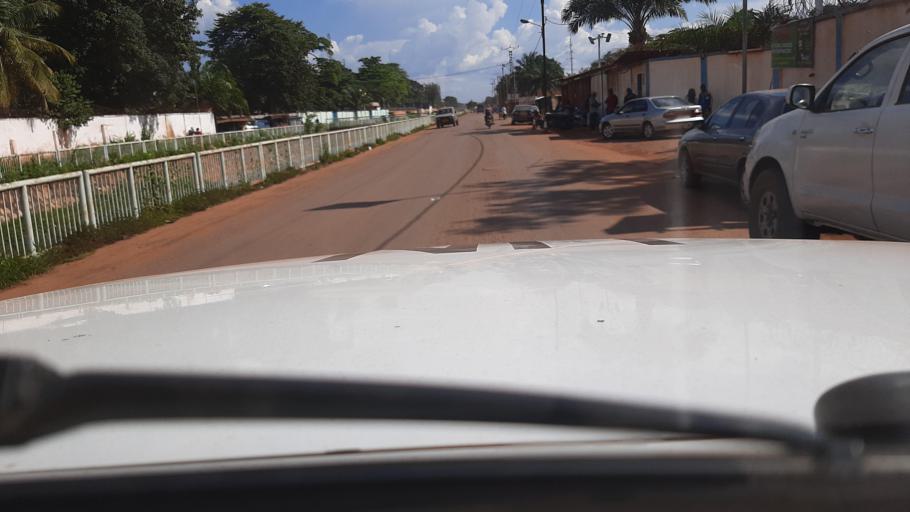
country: CF
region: Bangui
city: Bangui
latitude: 4.3703
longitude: 18.5522
